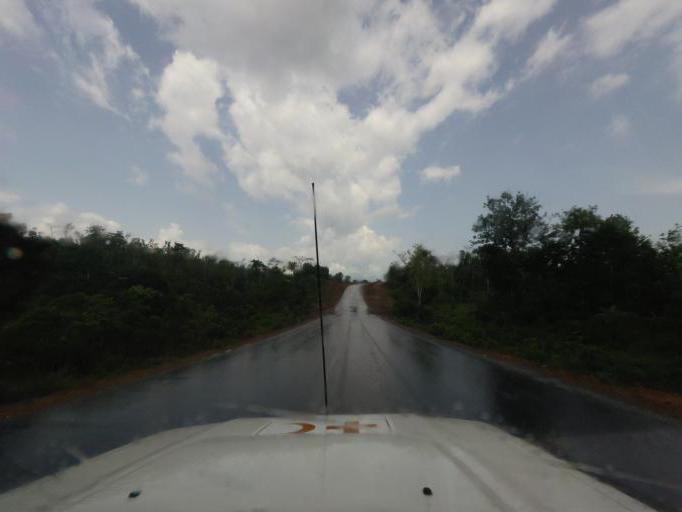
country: LR
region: Margibi
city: Kakata
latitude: 6.7817
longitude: -9.9646
